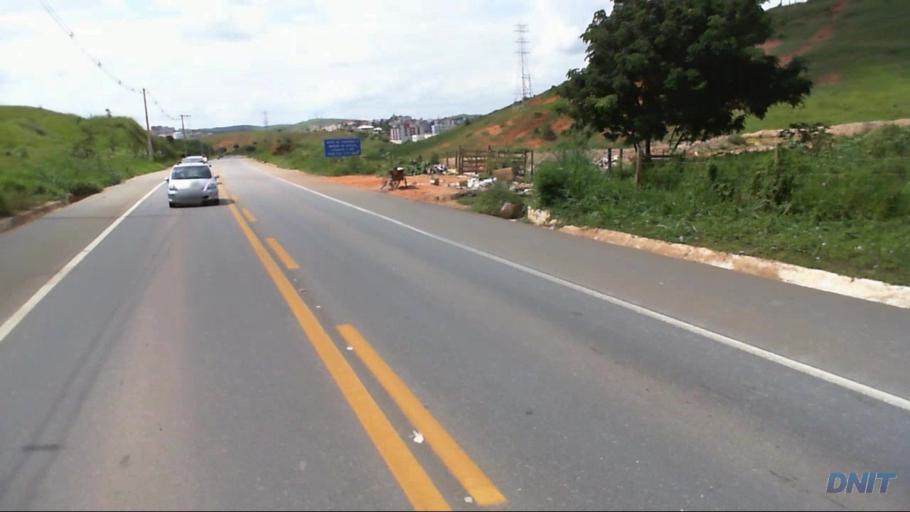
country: BR
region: Minas Gerais
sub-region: Governador Valadares
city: Governador Valadares
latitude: -18.8435
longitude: -41.9723
